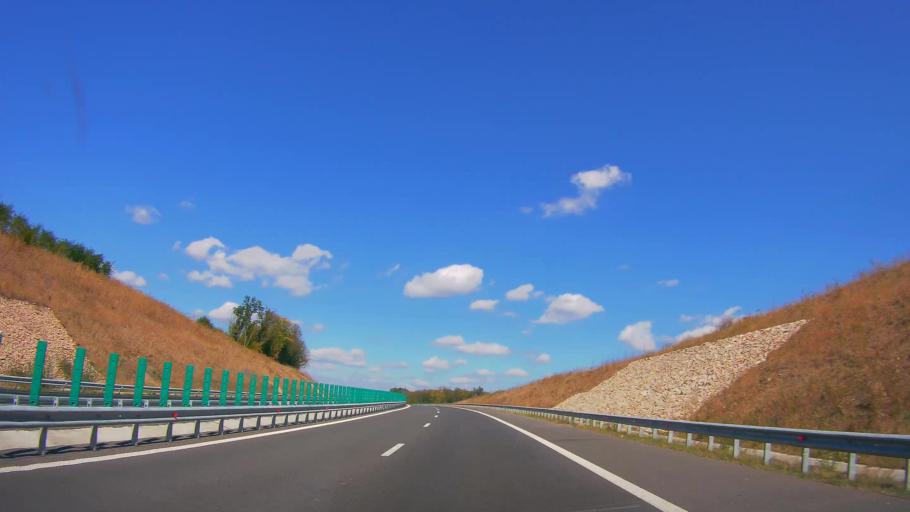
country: RO
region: Cluj
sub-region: Comuna Floresti
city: Luna de Sus
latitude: 46.7810
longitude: 23.4135
